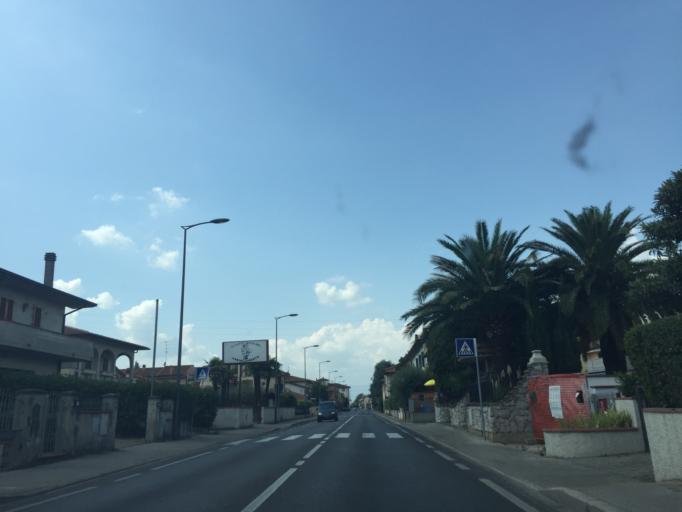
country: IT
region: Tuscany
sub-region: Provincia di Prato
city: Poggetto
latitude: 43.8262
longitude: 11.0422
